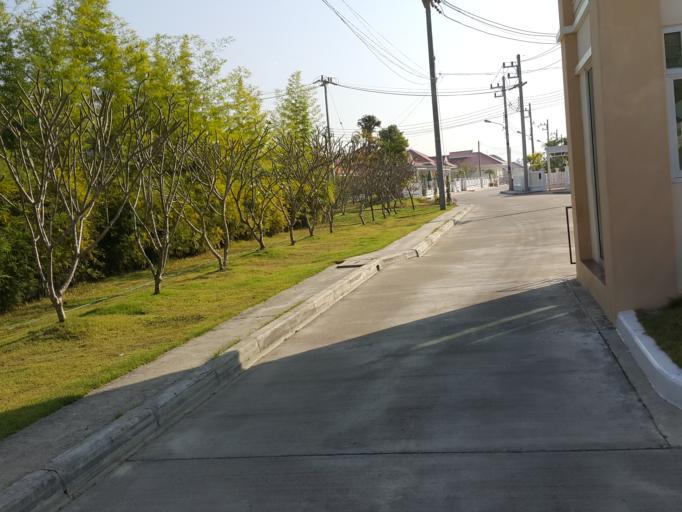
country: TH
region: Chiang Mai
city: San Kamphaeng
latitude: 18.7020
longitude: 99.1048
